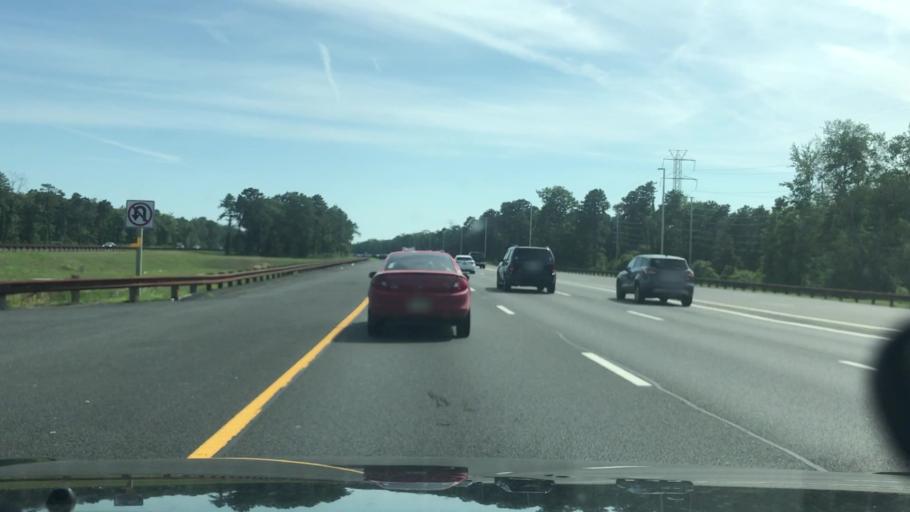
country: US
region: New Jersey
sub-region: Ocean County
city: Leisure Village
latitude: 40.0508
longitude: -74.1716
